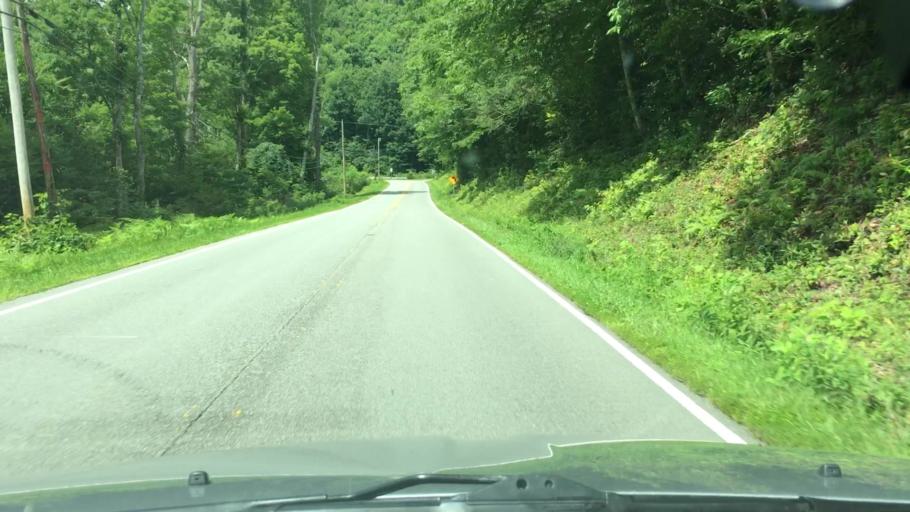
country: US
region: North Carolina
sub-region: Yancey County
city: Burnsville
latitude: 35.7934
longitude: -82.2016
